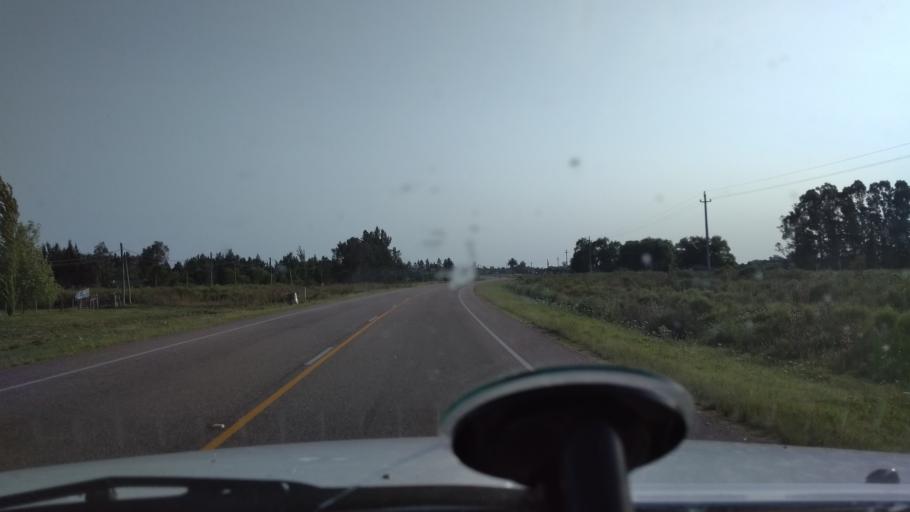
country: UY
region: Canelones
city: Sauce
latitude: -34.6525
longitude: -56.0519
